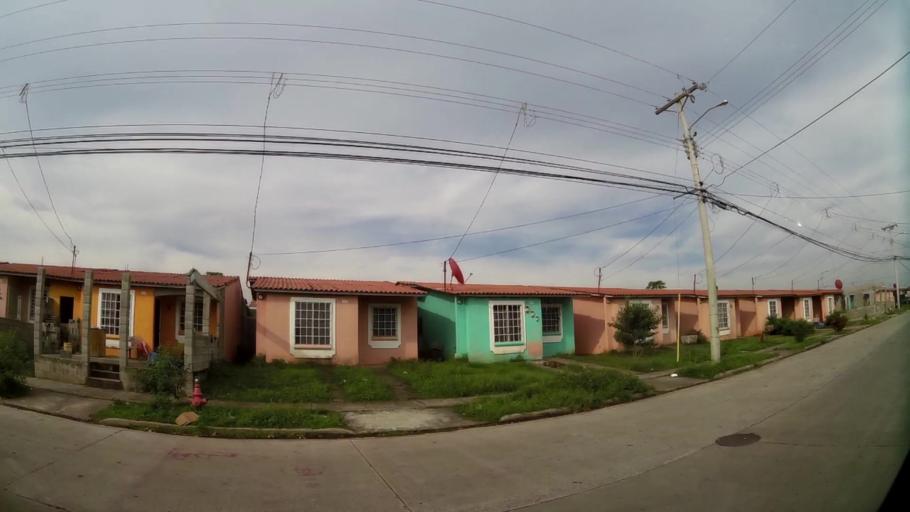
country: PA
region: Panama
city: Tocumen
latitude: 9.0690
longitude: -79.3626
